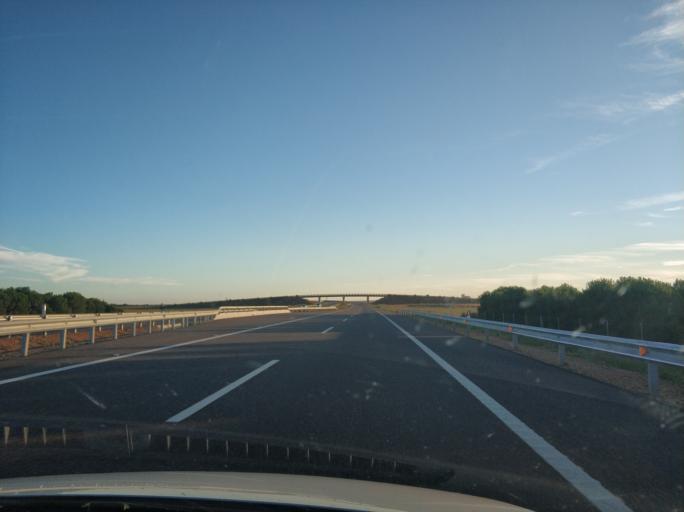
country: ES
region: Castille and Leon
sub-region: Provincia de Zamora
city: Barcial del Barco
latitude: 41.9496
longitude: -5.6268
